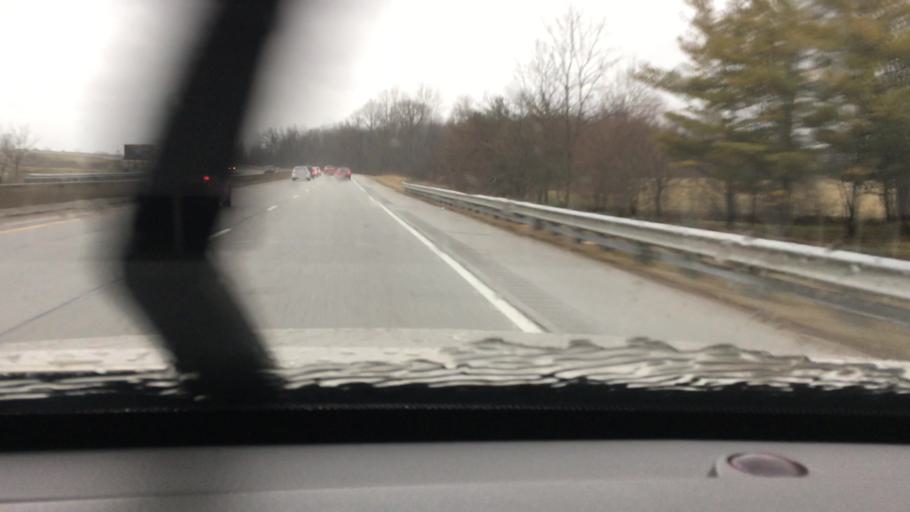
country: US
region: Indiana
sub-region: Delaware County
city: Yorktown
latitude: 40.2210
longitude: -85.5208
